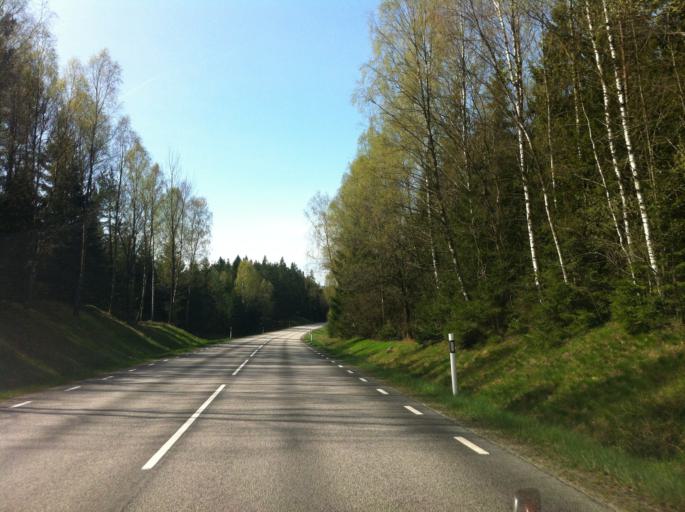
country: SE
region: Vaestra Goetaland
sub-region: Marks Kommun
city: Fritsla
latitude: 57.3193
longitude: 12.8921
